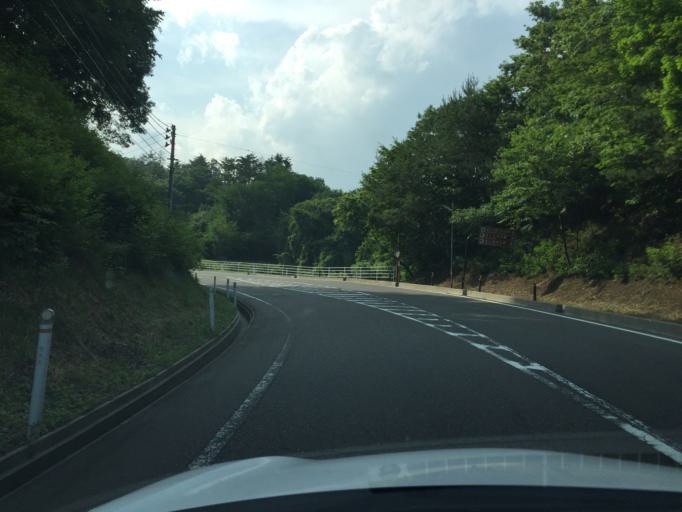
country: JP
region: Fukushima
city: Miharu
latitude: 37.3969
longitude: 140.4814
